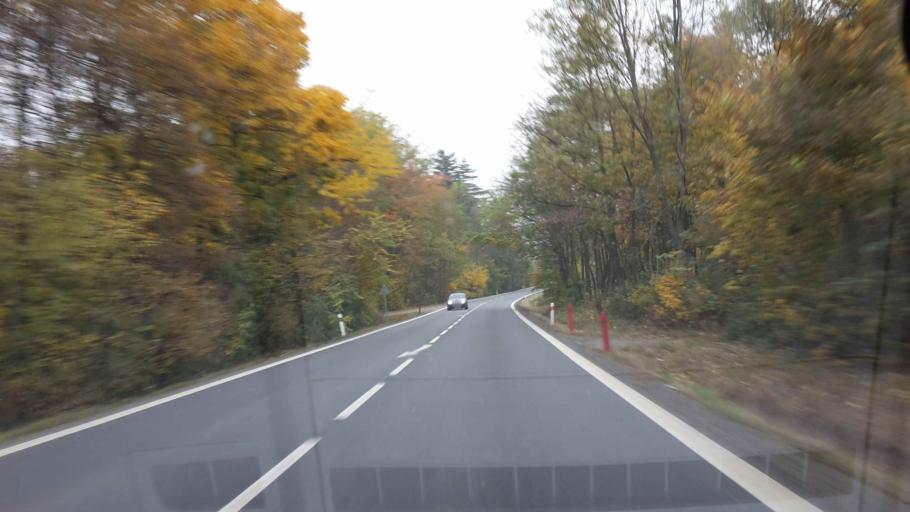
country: CZ
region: South Moravian
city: Damborice
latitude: 49.0945
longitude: 16.9150
